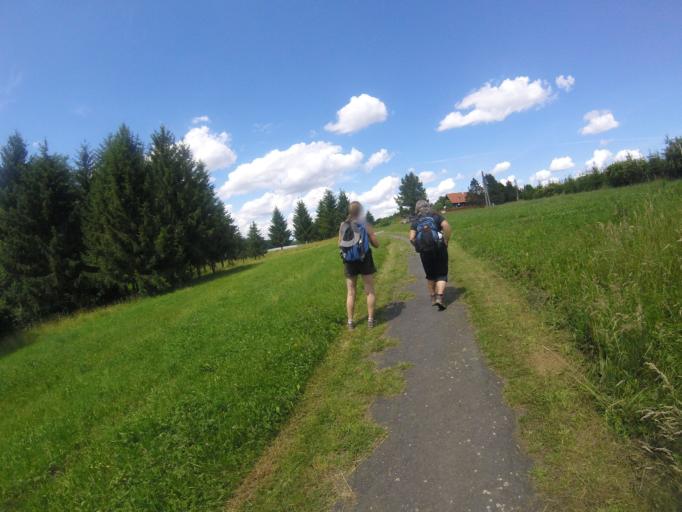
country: HU
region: Zala
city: Zalalovo
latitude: 46.8483
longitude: 16.5686
